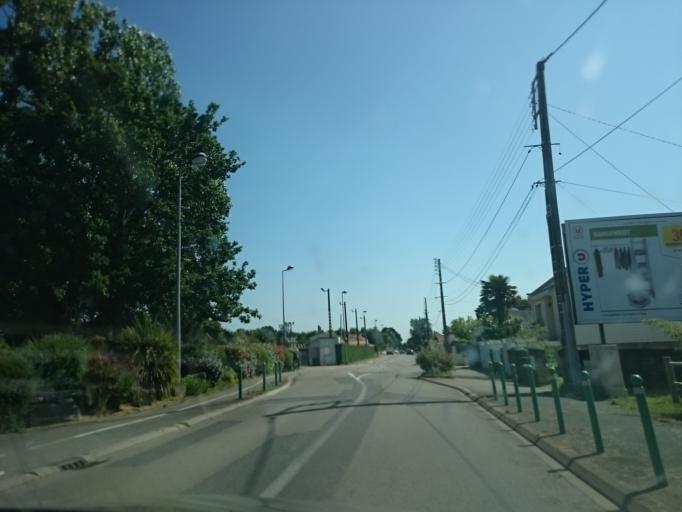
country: FR
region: Pays de la Loire
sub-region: Departement de la Loire-Atlantique
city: La Montagne
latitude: 47.1823
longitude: -1.6760
